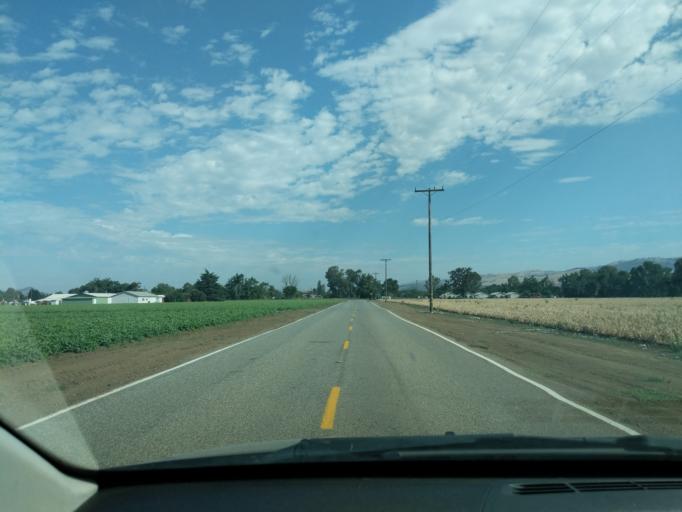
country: US
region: California
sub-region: Santa Clara County
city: Gilroy
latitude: 37.0451
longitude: -121.5611
